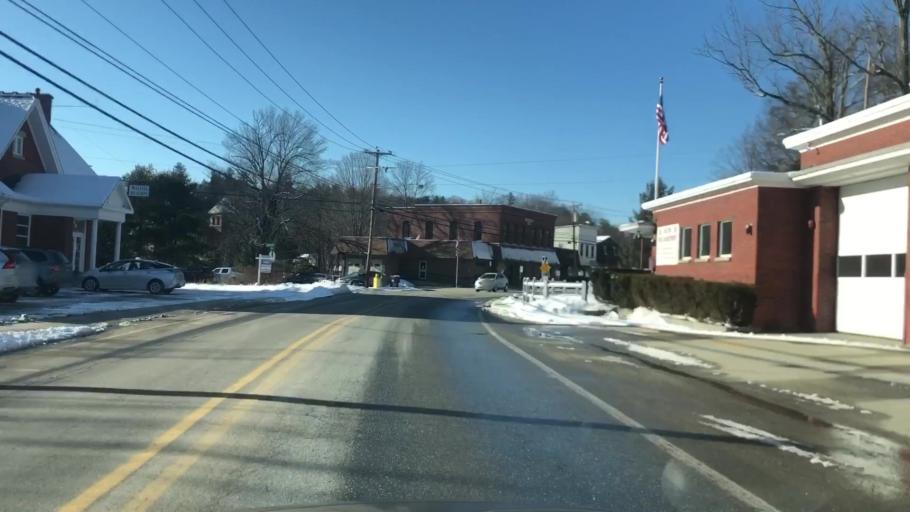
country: US
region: New Hampshire
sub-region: Hillsborough County
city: Wilton
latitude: 42.8423
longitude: -71.7361
